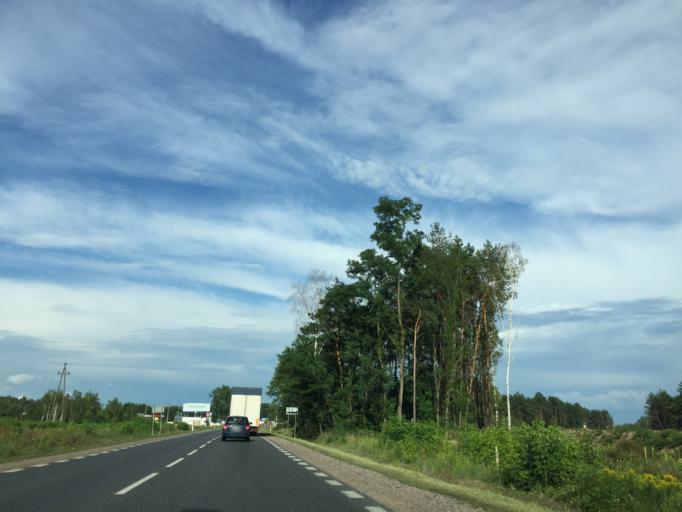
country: PL
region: Masovian Voivodeship
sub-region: Powiat piaseczynski
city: Gora Kalwaria
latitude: 51.9706
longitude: 21.1946
